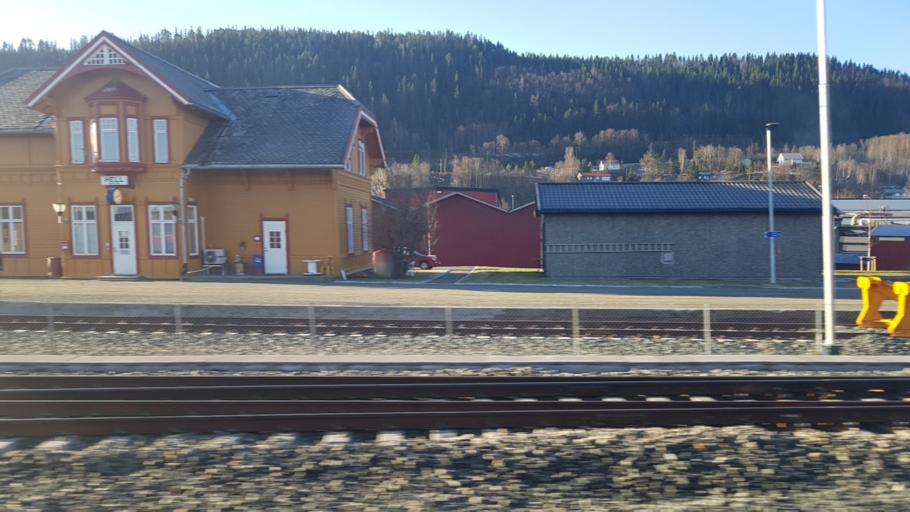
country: NO
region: Nord-Trondelag
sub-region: Stjordal
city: Stjordal
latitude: 63.4475
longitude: 10.9007
